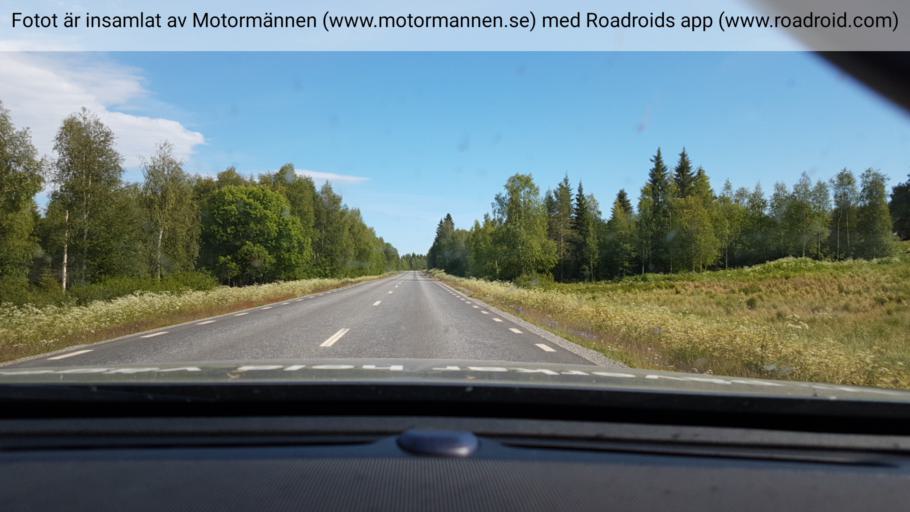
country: SE
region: Vaesterbotten
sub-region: Lycksele Kommun
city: Soderfors
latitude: 64.8214
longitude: 18.0624
